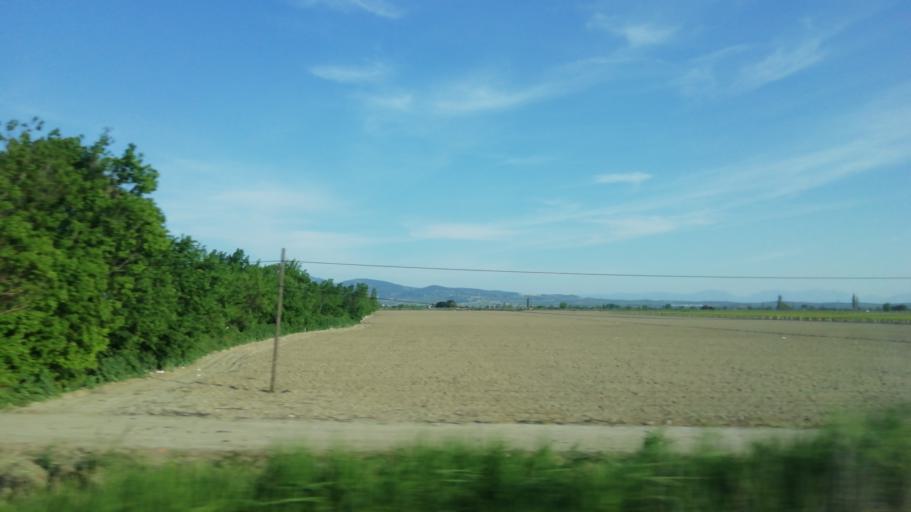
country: TR
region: Manisa
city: Saruhanli
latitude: 38.7435
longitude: 27.6086
